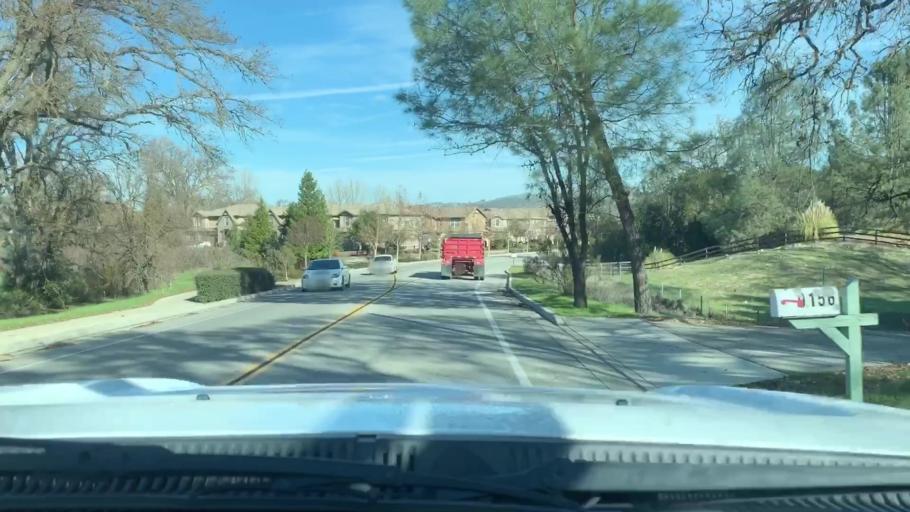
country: US
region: California
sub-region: San Luis Obispo County
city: Atascadero
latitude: 35.4449
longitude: -120.6370
